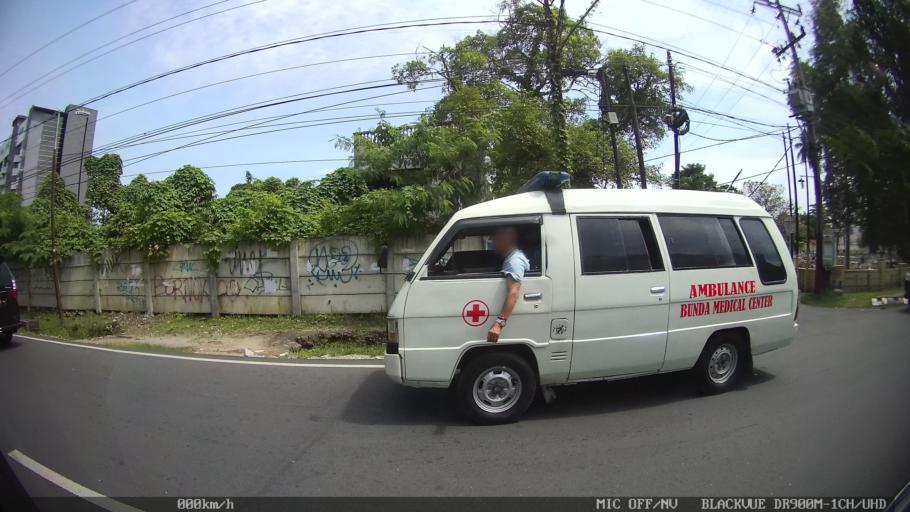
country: ID
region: North Sumatra
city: Medan
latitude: 3.5937
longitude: 98.6696
